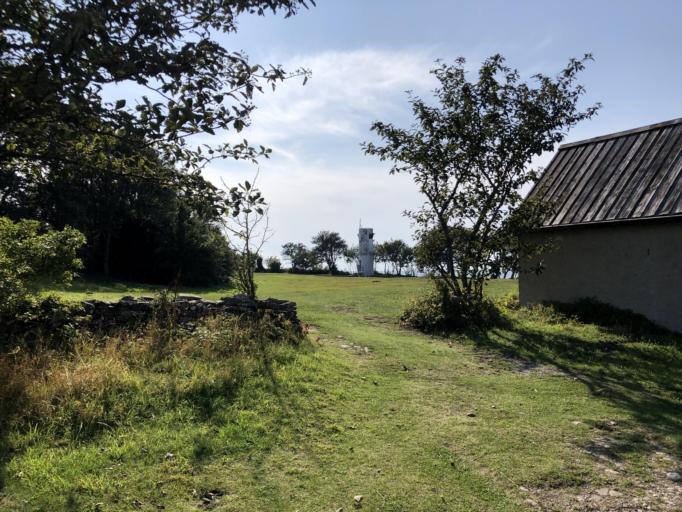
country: SE
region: Gotland
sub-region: Gotland
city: Hemse
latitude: 57.0308
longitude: 18.2196
